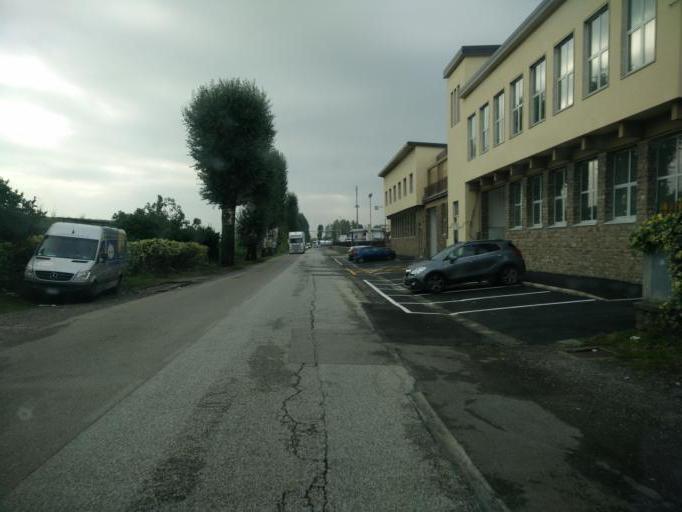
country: IT
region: Tuscany
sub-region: Province of Florence
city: Campi Bisenzio
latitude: 43.8498
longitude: 11.1229
